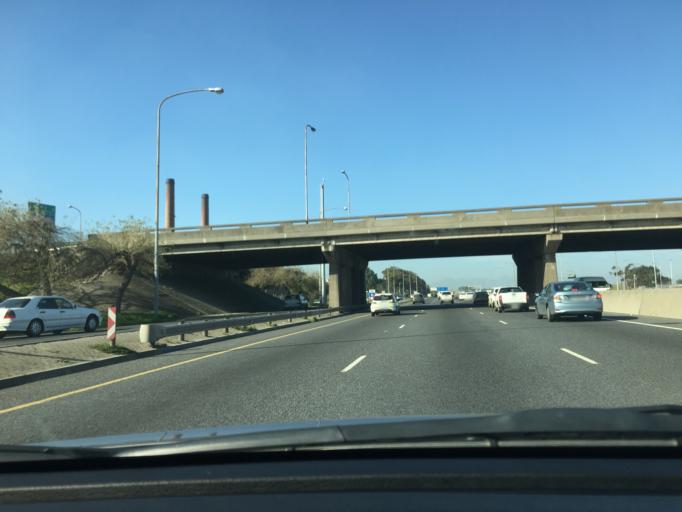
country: ZA
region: Western Cape
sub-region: City of Cape Town
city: Rosebank
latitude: -33.9498
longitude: 18.5079
